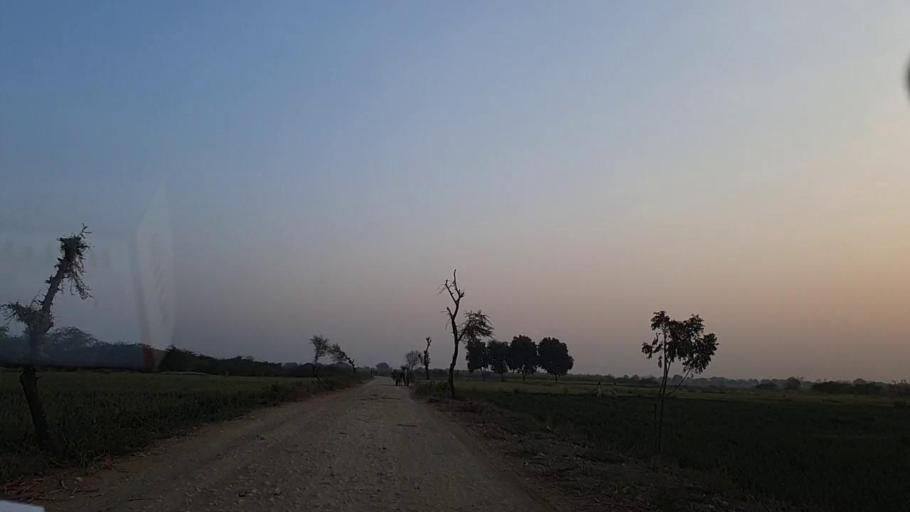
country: PK
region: Sindh
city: Tando Ghulam Ali
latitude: 25.1645
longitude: 68.9219
